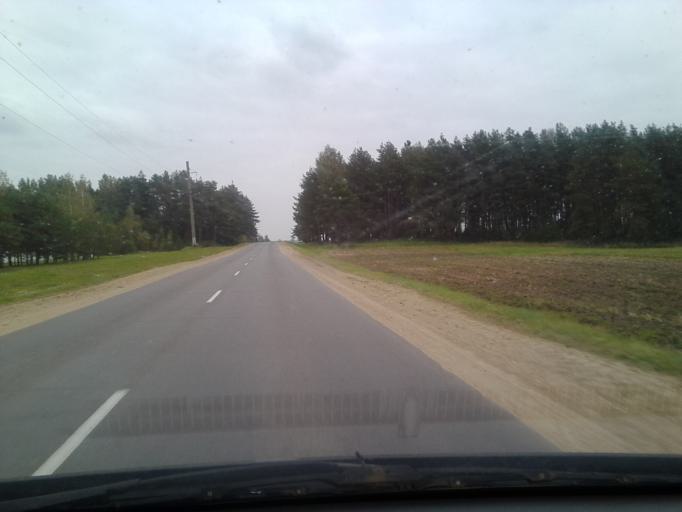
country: BY
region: Vitebsk
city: Pastavy
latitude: 55.1122
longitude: 26.8853
